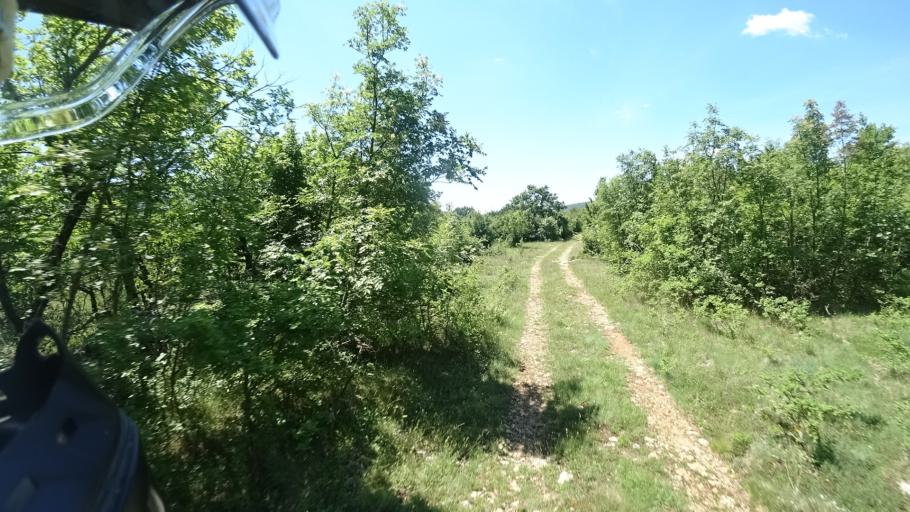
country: HR
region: Sibensko-Kniniska
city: Knin
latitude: 44.0056
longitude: 16.3099
